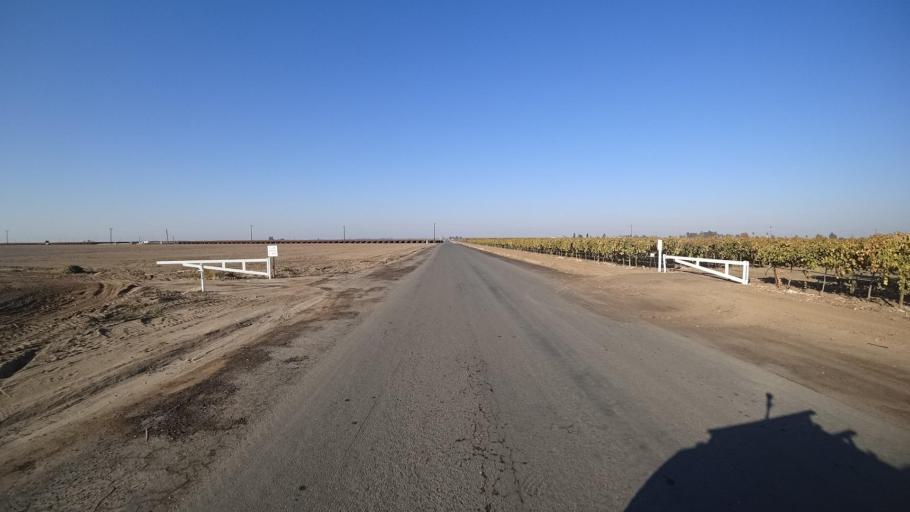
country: US
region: California
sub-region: Tulare County
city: Richgrove
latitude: 35.7669
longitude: -119.1645
